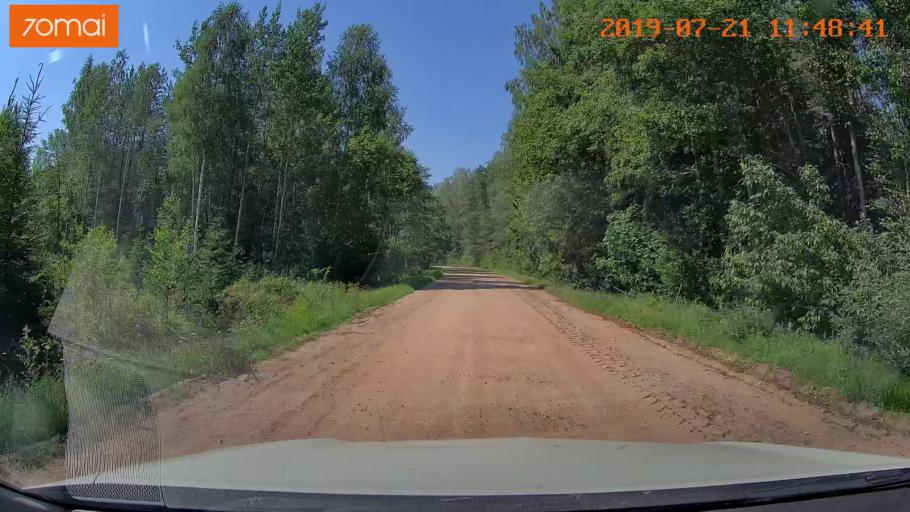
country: BY
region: Grodnenskaya
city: Lyubcha
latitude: 53.8964
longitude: 26.0472
